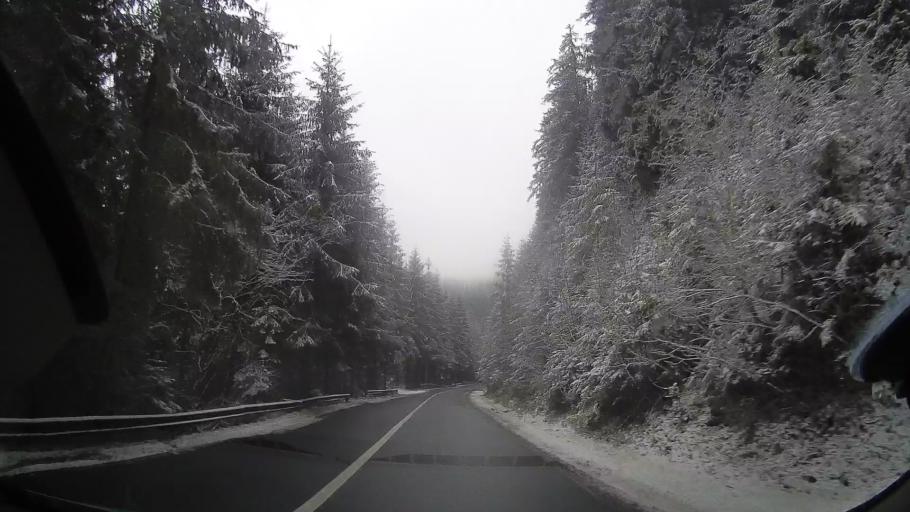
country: RO
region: Cluj
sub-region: Comuna Belis
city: Belis
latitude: 46.6509
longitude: 23.0492
